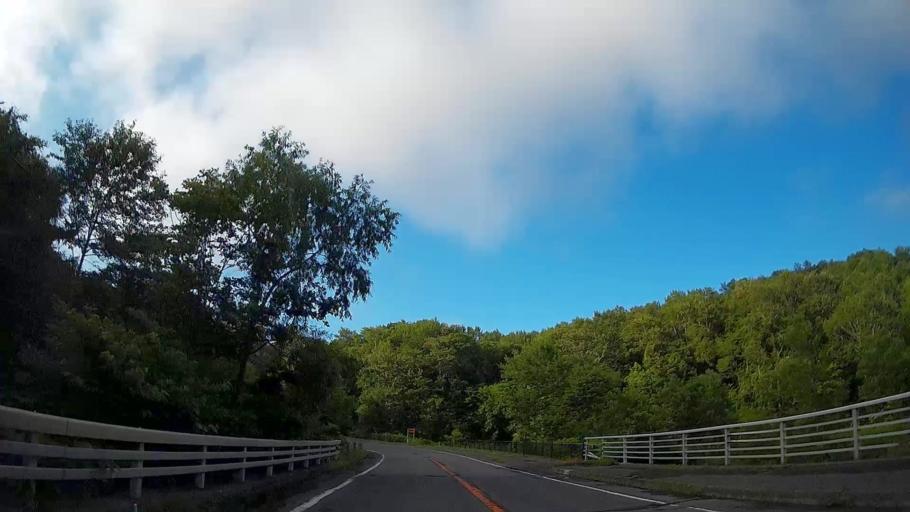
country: JP
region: Hokkaido
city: Date
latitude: 42.5440
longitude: 140.8574
